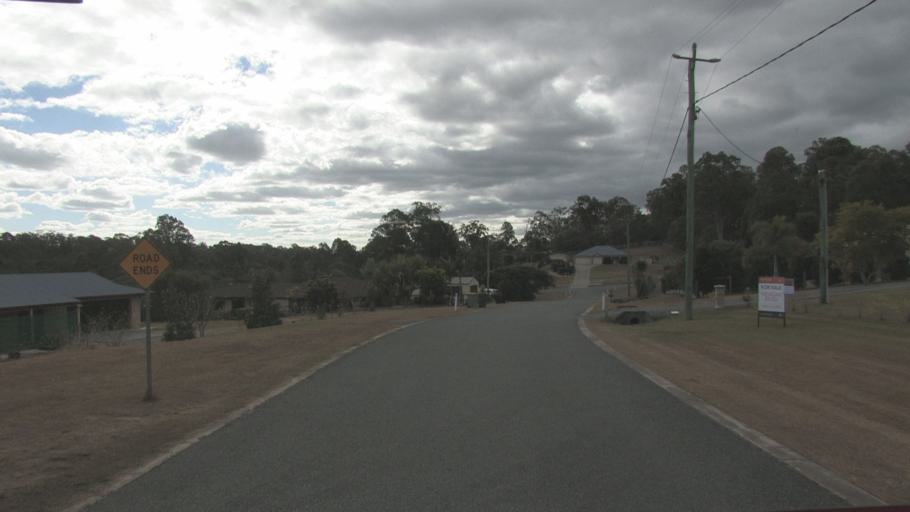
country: AU
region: Queensland
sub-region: Logan
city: Cedar Vale
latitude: -27.8834
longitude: 153.0135
